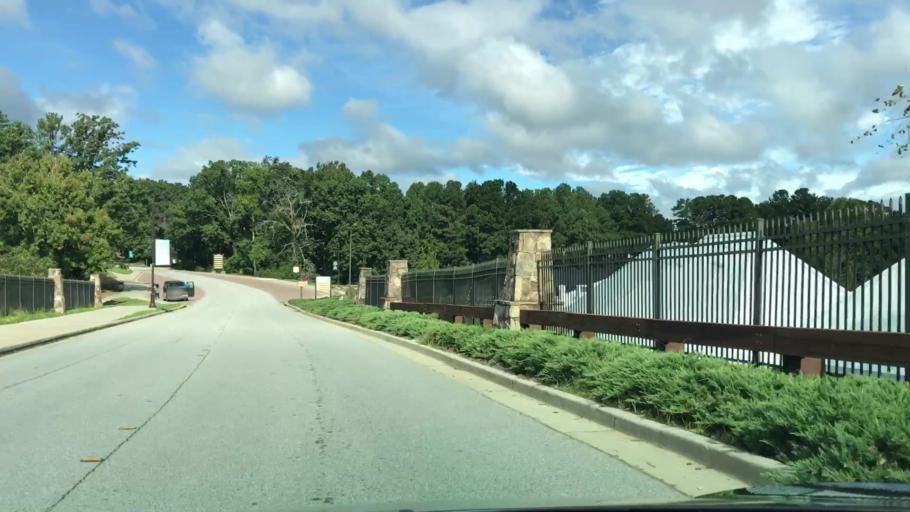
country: US
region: Georgia
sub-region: Gwinnett County
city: Buford
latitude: 34.1776
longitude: -84.0295
